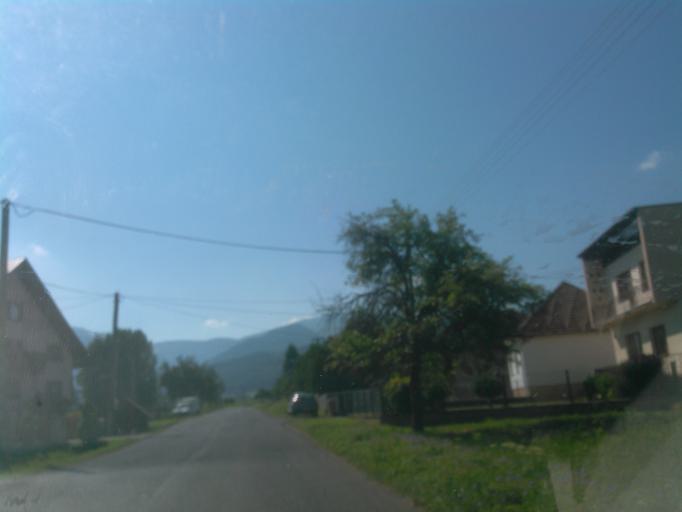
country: SK
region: Zilinsky
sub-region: Okres Liptovsky Mikulas
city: Liptovsky Mikulas
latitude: 49.0333
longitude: 19.5030
